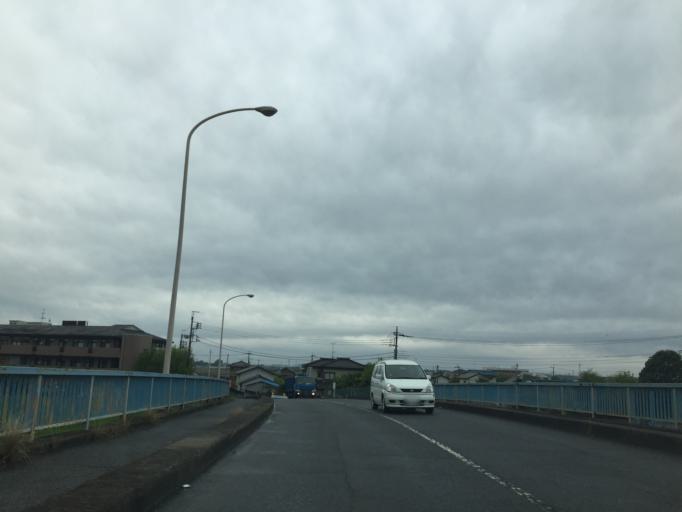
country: JP
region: Saitama
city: Shiki
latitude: 35.8725
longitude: 139.5630
